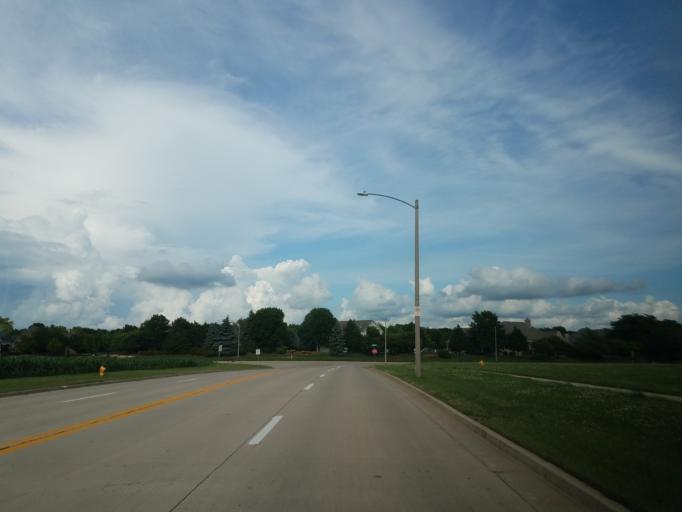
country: US
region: Illinois
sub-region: McLean County
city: Normal
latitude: 40.5075
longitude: -88.9433
